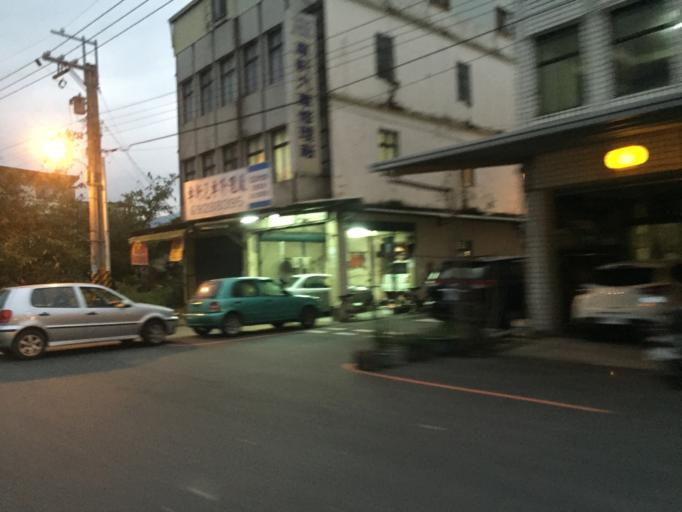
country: TW
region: Taiwan
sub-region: Yilan
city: Yilan
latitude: 24.7596
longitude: 121.7393
